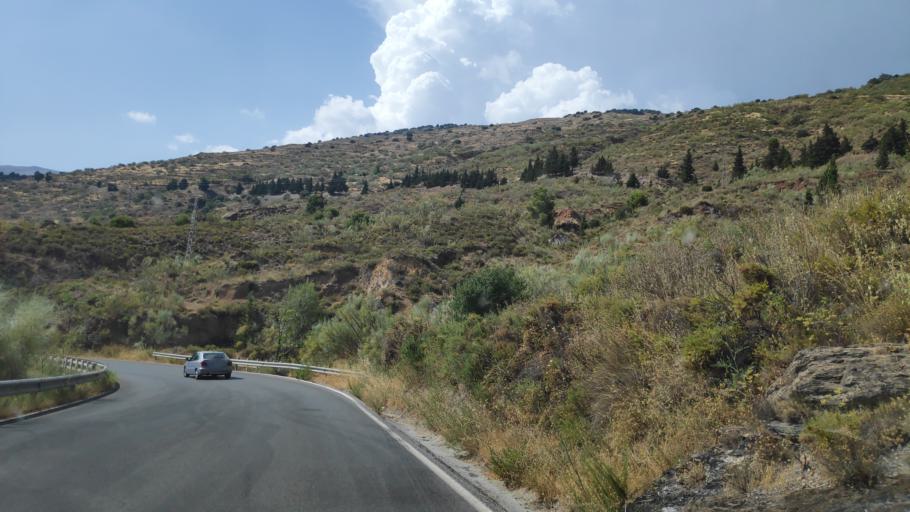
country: ES
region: Andalusia
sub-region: Provincia de Granada
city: Soportujar
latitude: 36.9228
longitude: -3.3891
